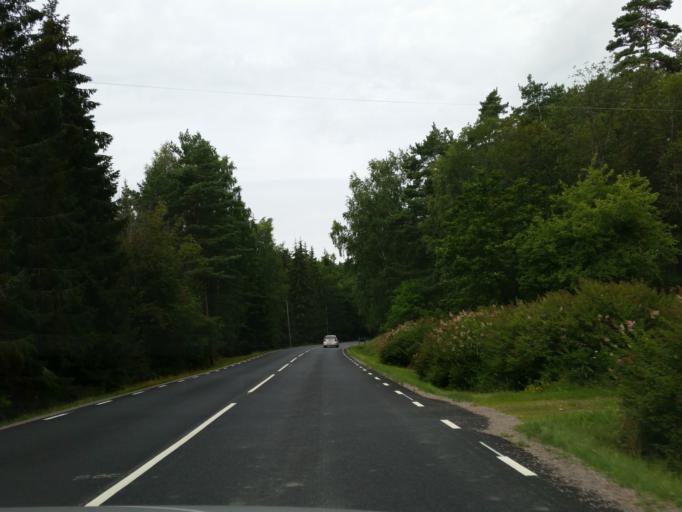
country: SE
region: Soedermanland
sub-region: Strangnas Kommun
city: Mariefred
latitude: 59.2624
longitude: 17.1652
